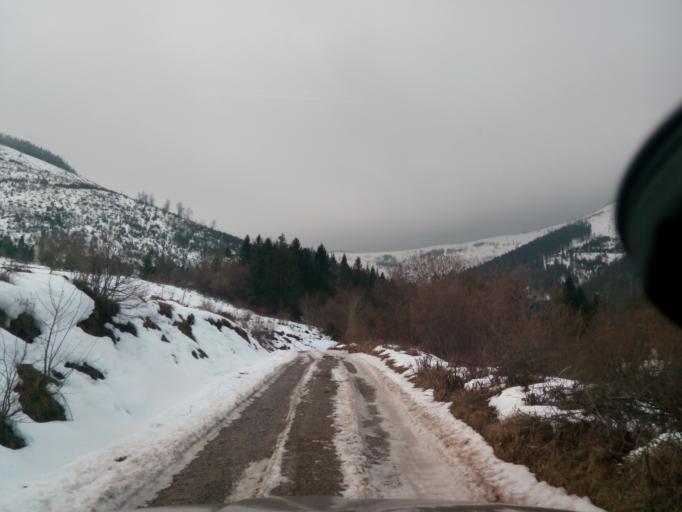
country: SK
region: Presovsky
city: Stara L'ubovna
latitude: 49.2147
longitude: 20.7477
